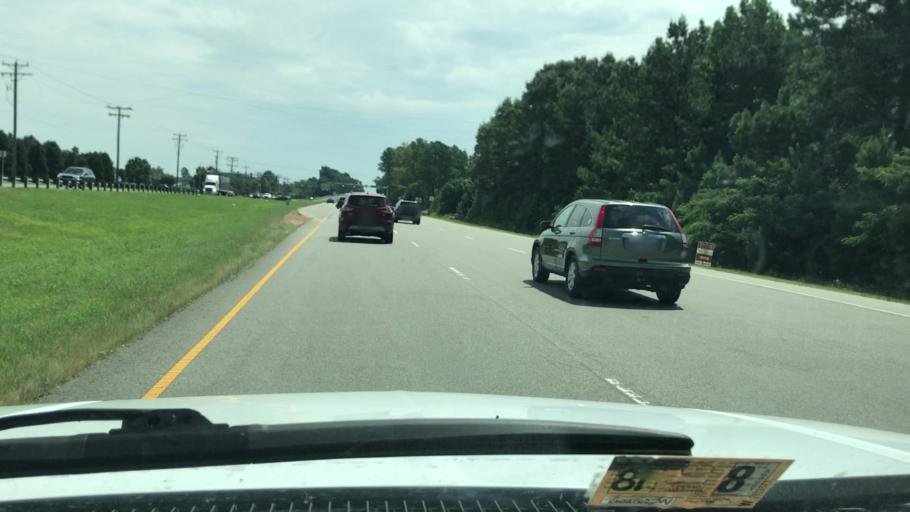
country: US
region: Virginia
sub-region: Chesterfield County
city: Brandermill
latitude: 37.5087
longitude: -77.6802
